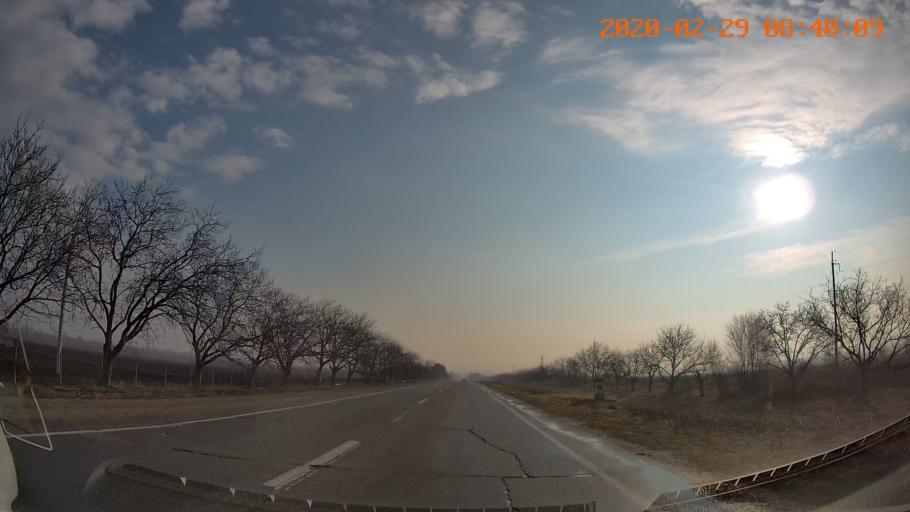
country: MD
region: Anenii Noi
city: Varnita
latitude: 46.9231
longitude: 29.4121
